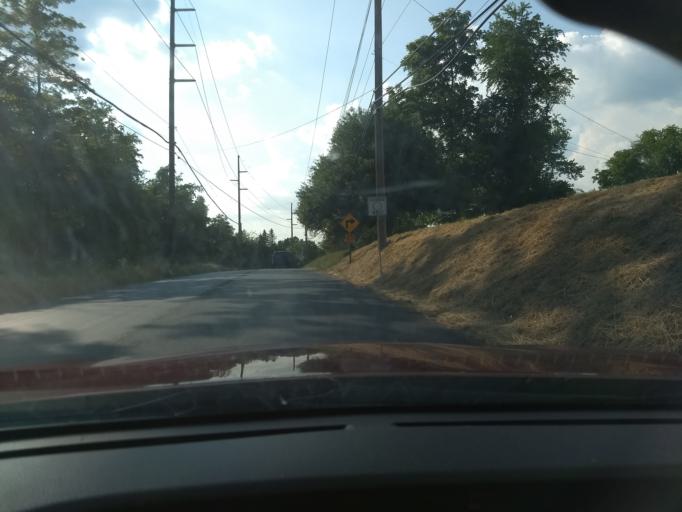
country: US
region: Pennsylvania
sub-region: Allegheny County
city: Plum
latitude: 40.4781
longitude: -79.7364
